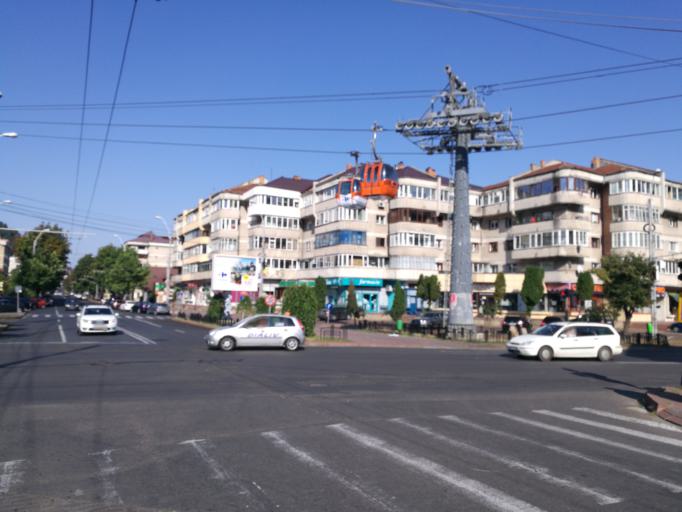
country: RO
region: Neamt
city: Piatra Neamt
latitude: 46.9277
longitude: 26.3612
